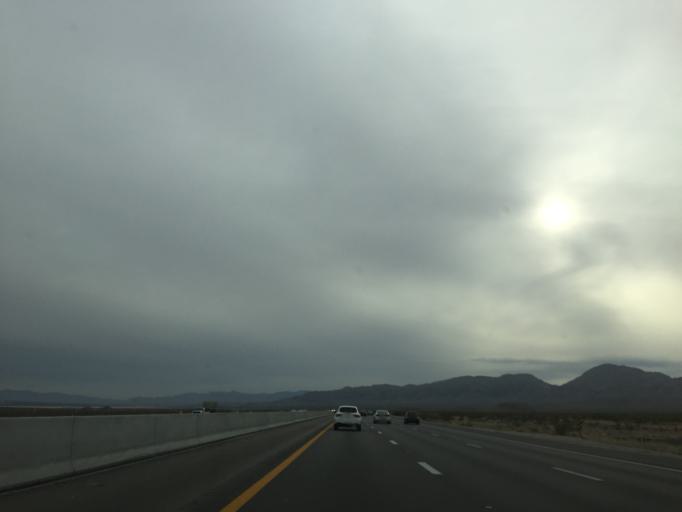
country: US
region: Nevada
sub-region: Clark County
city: Enterprise
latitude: 35.7637
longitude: -115.3410
